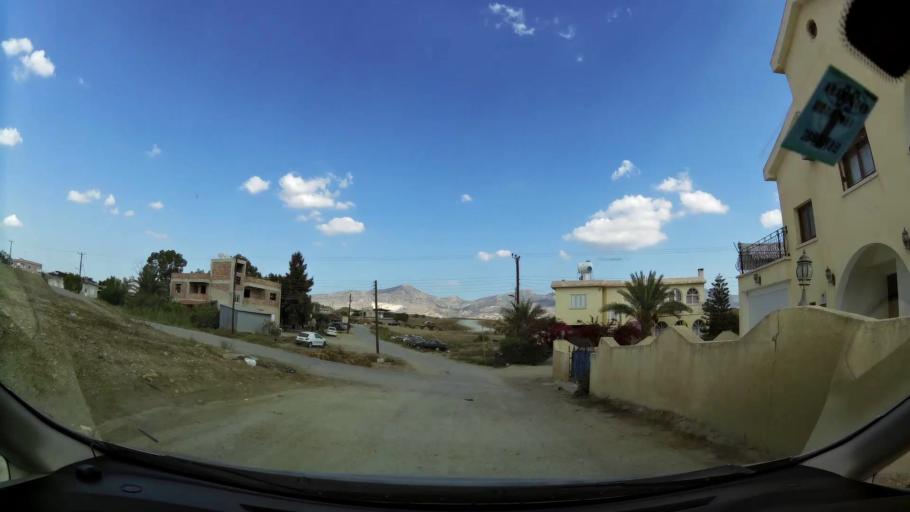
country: CY
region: Lefkosia
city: Nicosia
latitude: 35.2261
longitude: 33.3808
